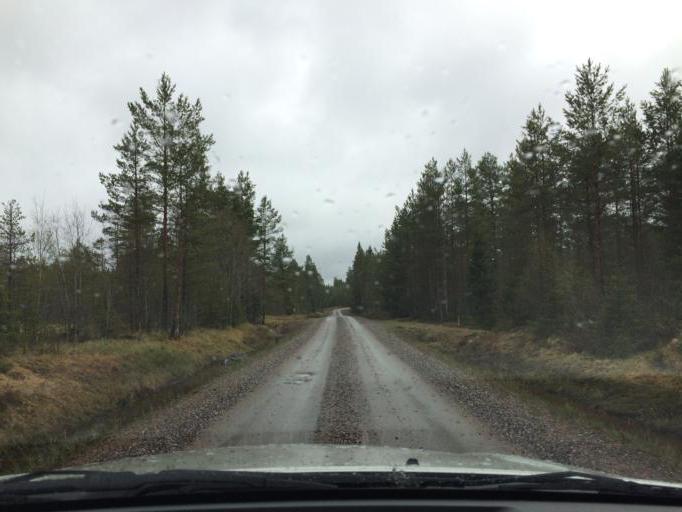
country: SE
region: OErebro
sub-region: Hallefors Kommun
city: Haellefors
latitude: 60.0301
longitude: 14.5540
